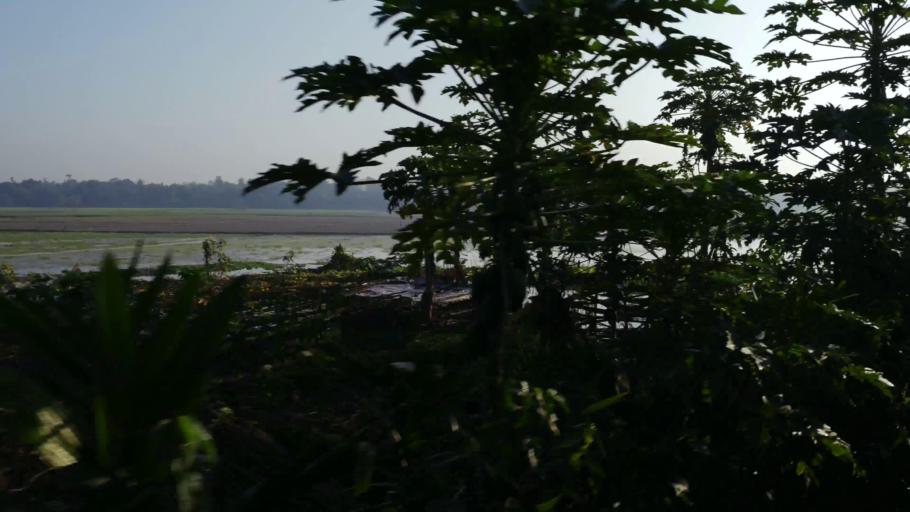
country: BD
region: Dhaka
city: Jamalpur
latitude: 24.9179
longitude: 89.9454
